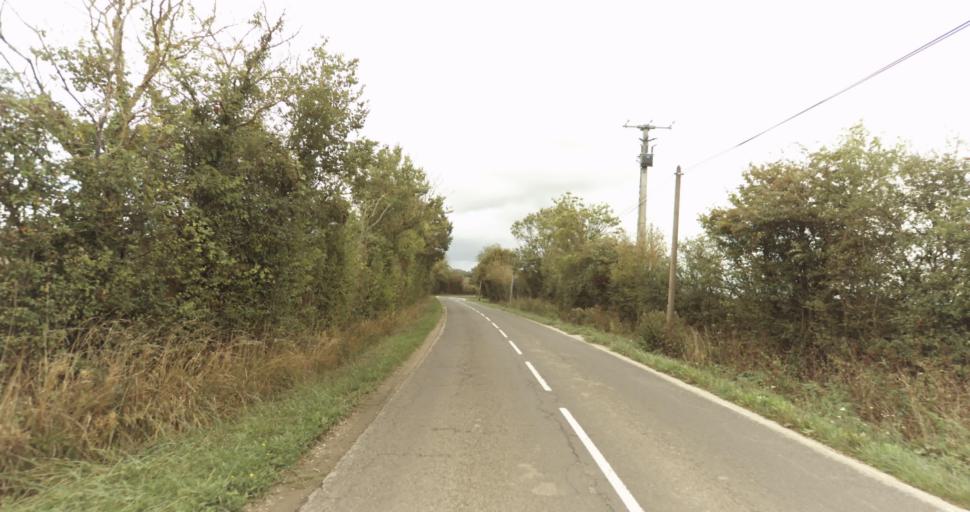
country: FR
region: Lower Normandy
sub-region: Departement de l'Orne
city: Gace
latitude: 48.7073
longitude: 0.3110
